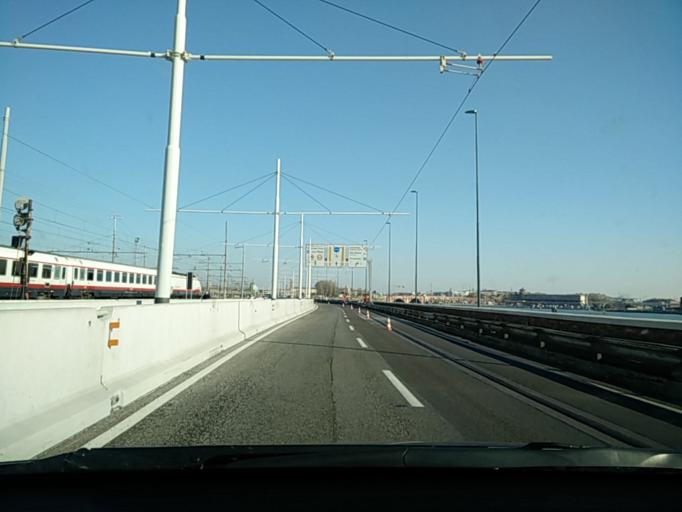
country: IT
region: Veneto
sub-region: Provincia di Venezia
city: Venice
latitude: 45.4474
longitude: 12.3099
